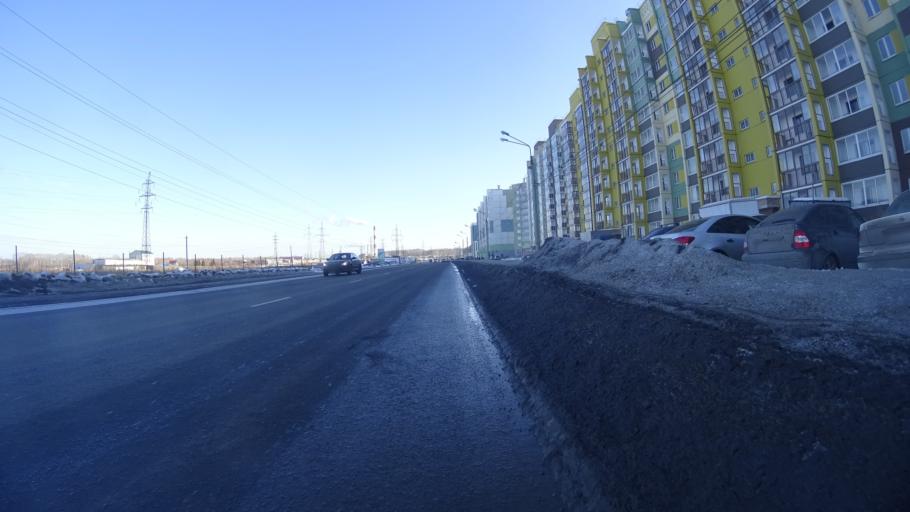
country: RU
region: Chelyabinsk
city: Roshchino
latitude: 55.2170
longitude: 61.3015
